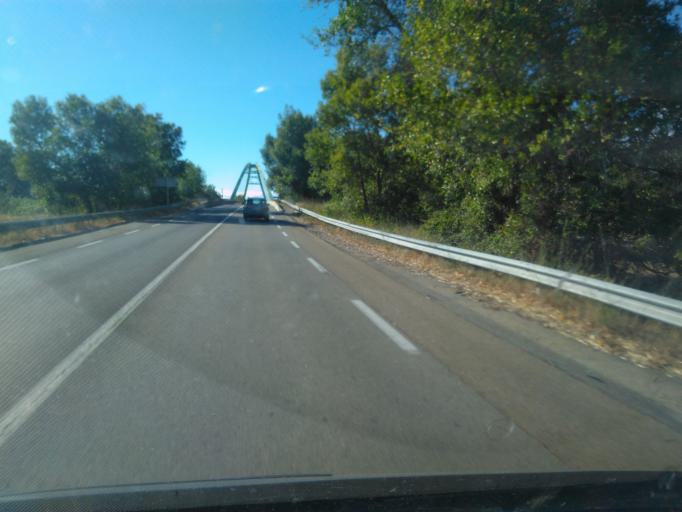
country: FR
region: Languedoc-Roussillon
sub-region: Departement du Gard
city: Saint-Gilles
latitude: 43.6640
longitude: 4.4552
